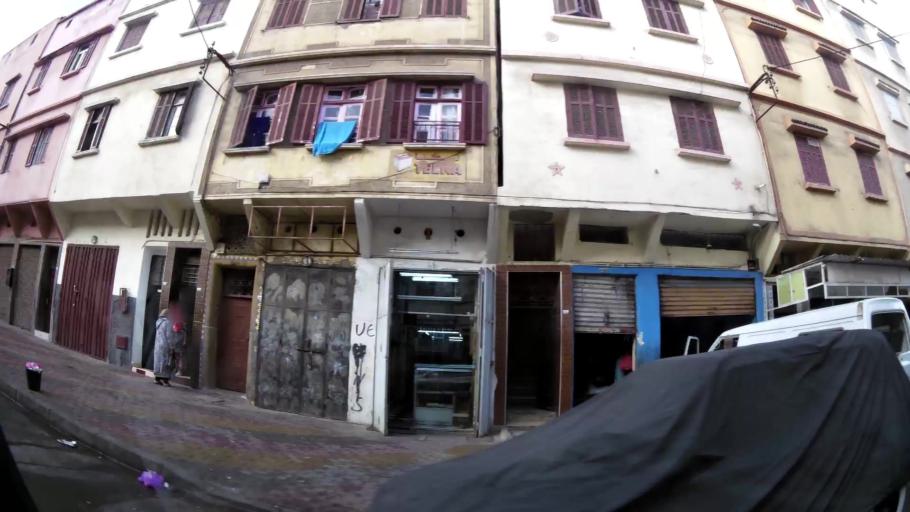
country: MA
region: Grand Casablanca
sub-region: Casablanca
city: Casablanca
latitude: 33.5692
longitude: -7.5822
